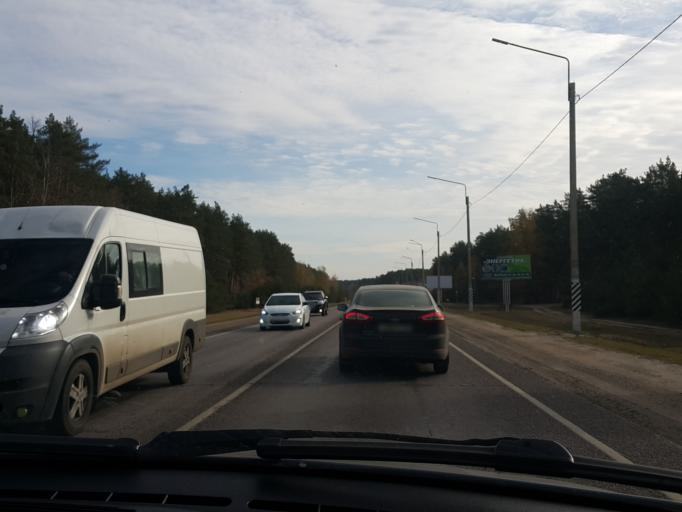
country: RU
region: Tambov
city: Donskoye
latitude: 52.7128
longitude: 41.5207
